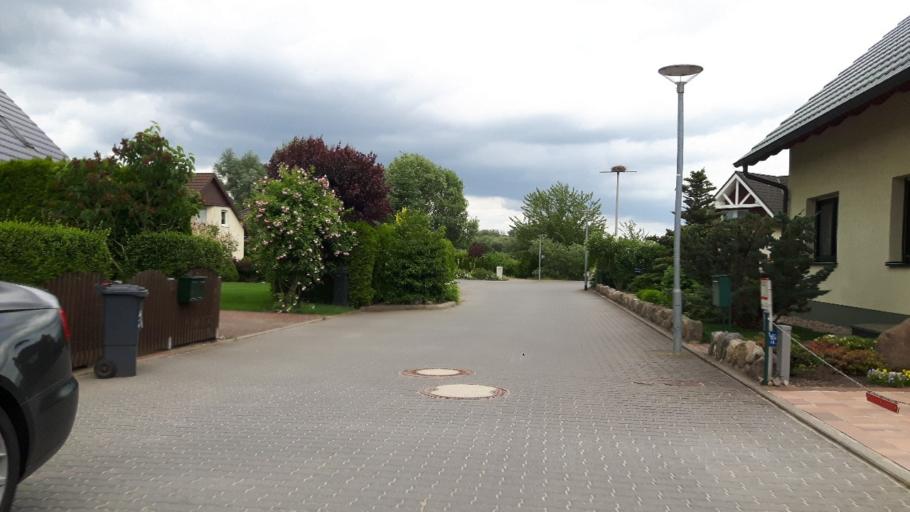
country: DE
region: Brandenburg
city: Schwedt (Oder)
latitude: 53.0576
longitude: 14.3012
